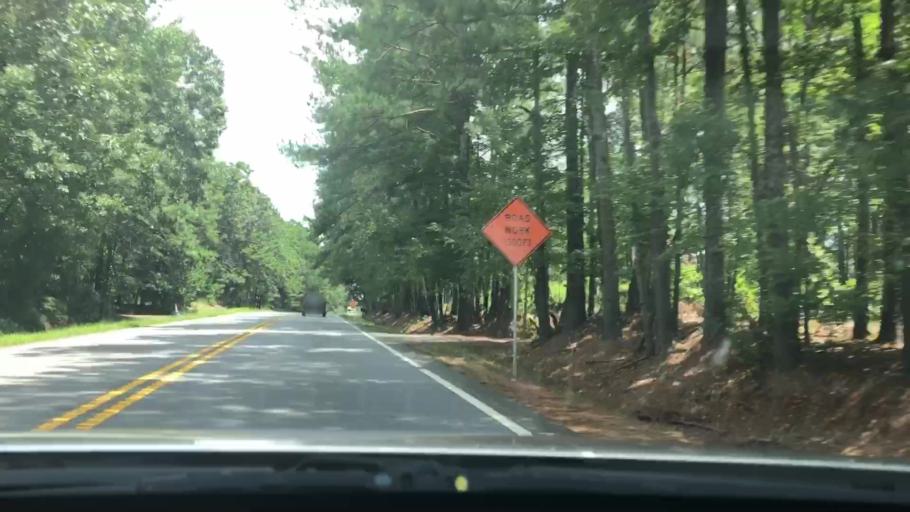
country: US
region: Georgia
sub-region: Lamar County
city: Barnesville
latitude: 33.1541
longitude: -84.1210
